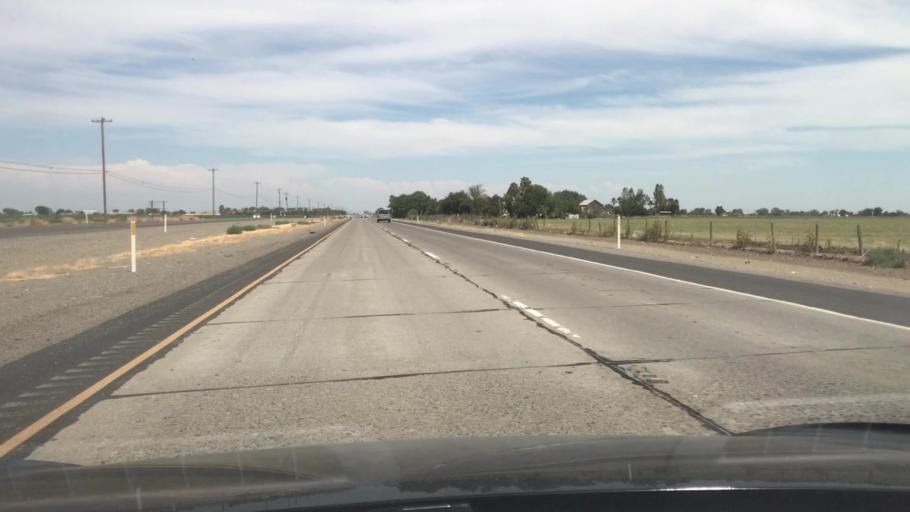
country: US
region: California
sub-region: Merced County
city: Los Banos
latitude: 37.0566
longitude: -120.9125
